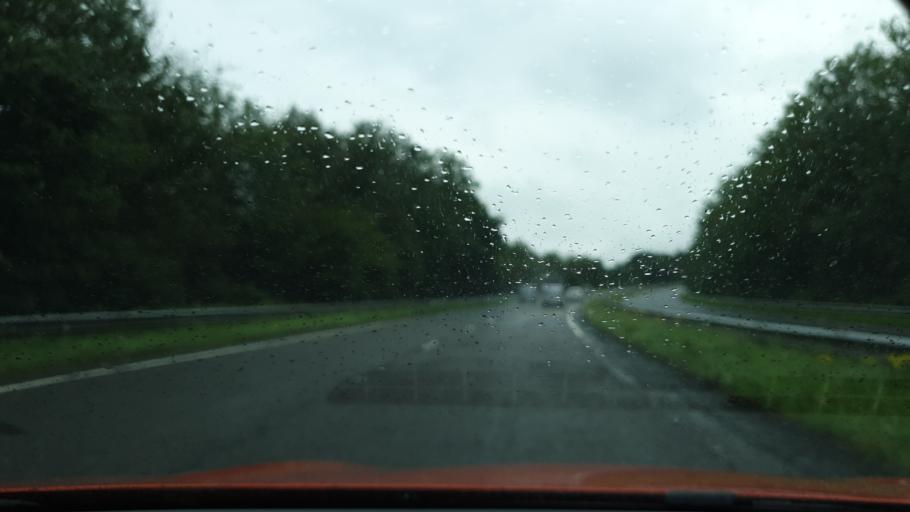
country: GB
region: England
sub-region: Cumbria
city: Grange-over-Sands
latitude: 54.2201
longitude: -2.8884
